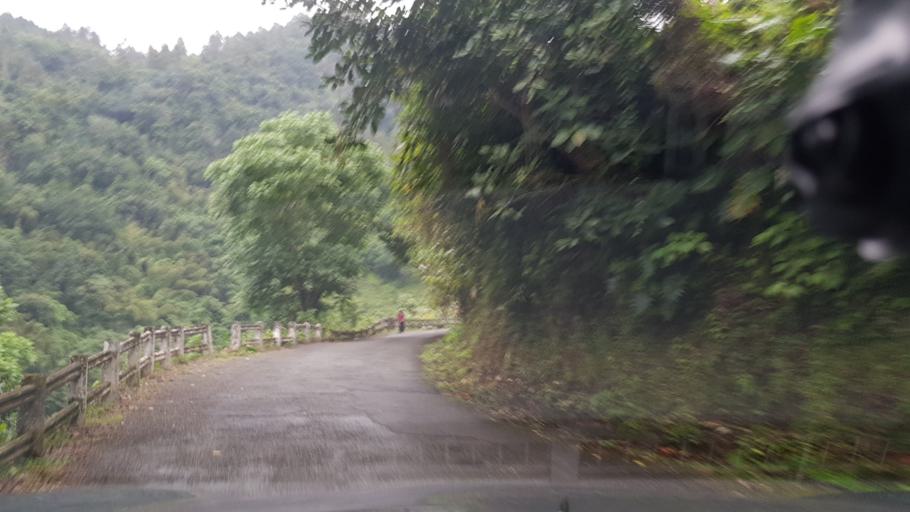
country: JM
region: Saint Andrew
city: Stony Hill
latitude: 18.1238
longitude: -76.7159
